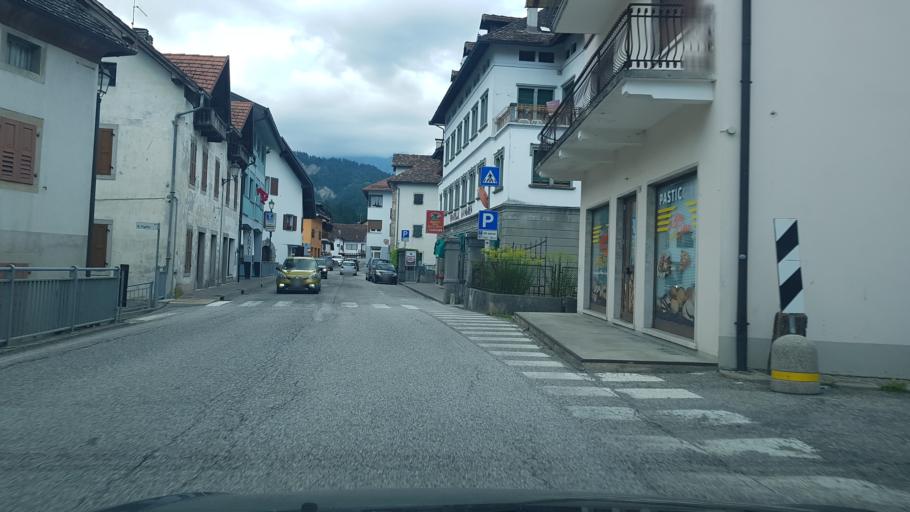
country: IT
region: Friuli Venezia Giulia
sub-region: Provincia di Udine
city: Ovaro
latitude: 46.4813
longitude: 12.8671
